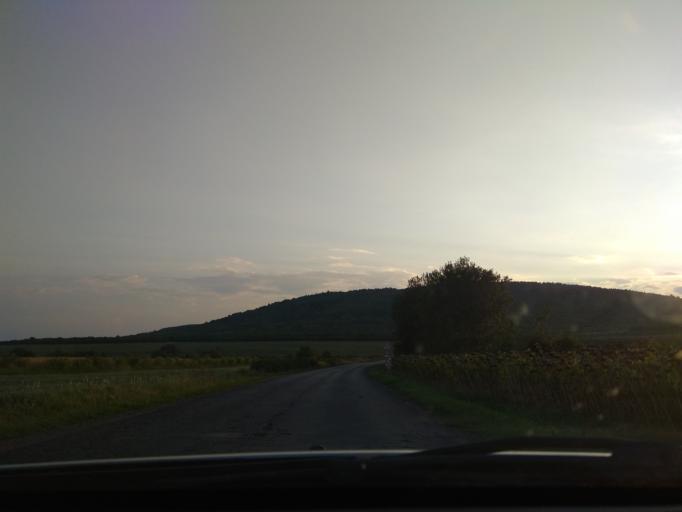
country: HU
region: Borsod-Abauj-Zemplen
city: Tallya
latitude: 48.2066
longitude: 21.2147
